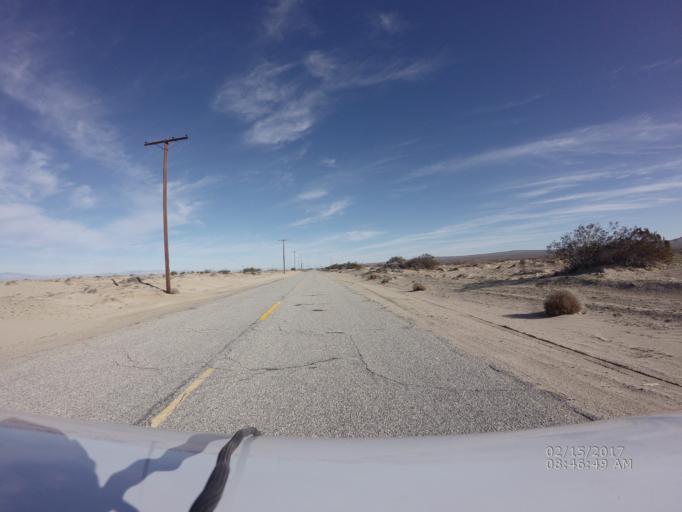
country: US
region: California
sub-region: Los Angeles County
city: Lake Los Angeles
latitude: 34.6861
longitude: -117.8807
